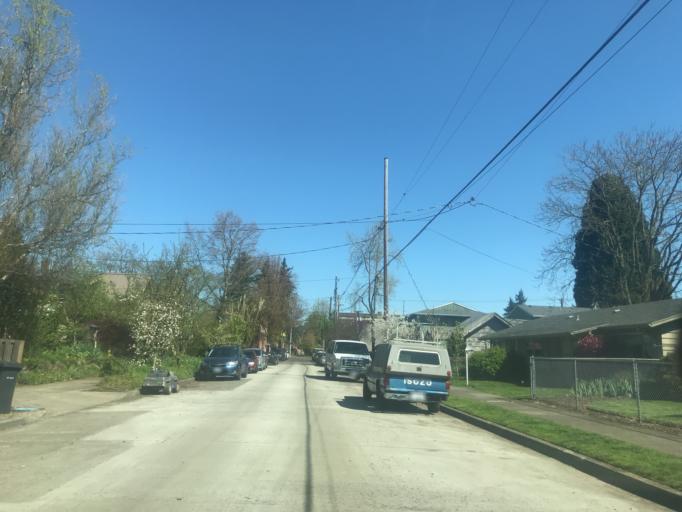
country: US
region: Oregon
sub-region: Multnomah County
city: Lents
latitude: 45.4884
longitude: -122.5970
